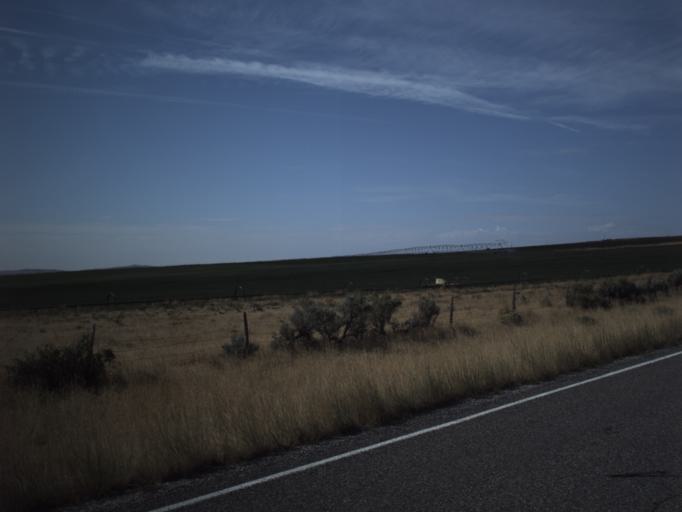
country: US
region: Idaho
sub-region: Minidoka County
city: Heyburn
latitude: 41.8204
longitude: -113.1949
